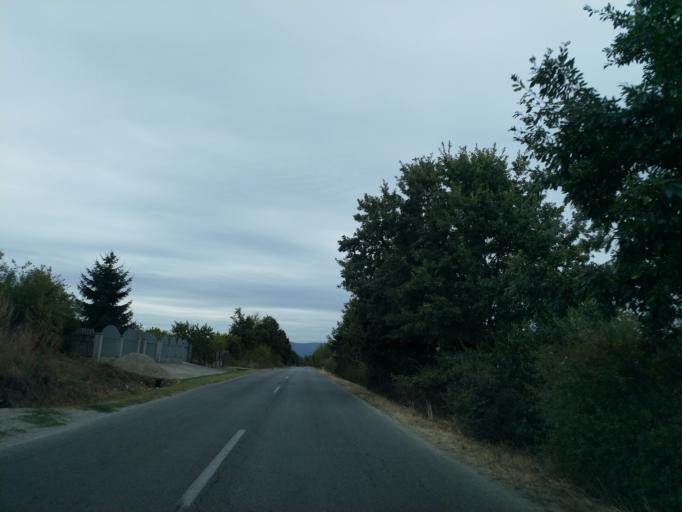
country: RS
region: Central Serbia
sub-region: Pomoravski Okrug
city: Jagodina
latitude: 44.0149
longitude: 21.1994
